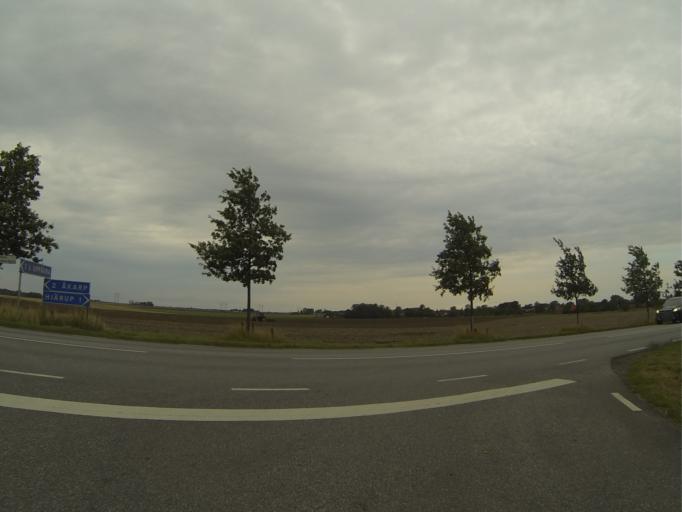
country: SE
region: Skane
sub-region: Staffanstorps Kommun
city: Hjaerup
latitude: 55.6601
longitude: 13.1423
